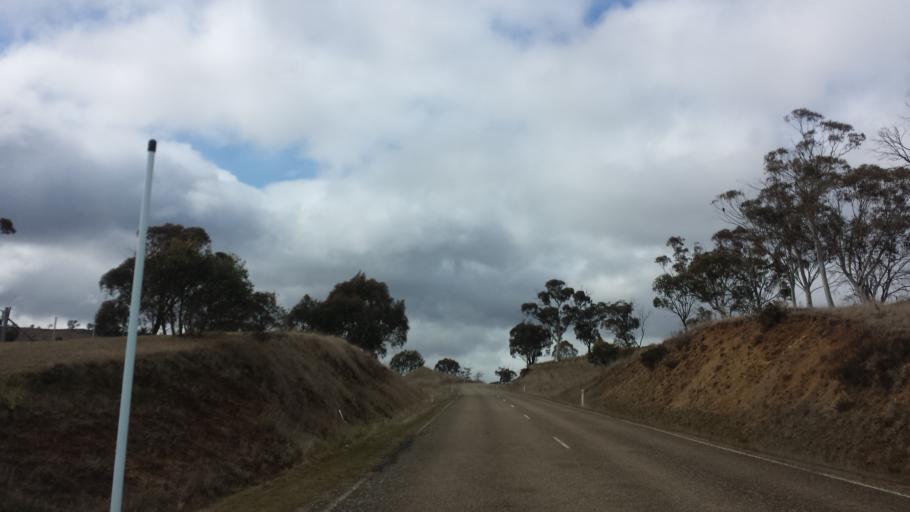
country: AU
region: Victoria
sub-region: Alpine
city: Mount Beauty
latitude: -37.0955
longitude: 147.4118
